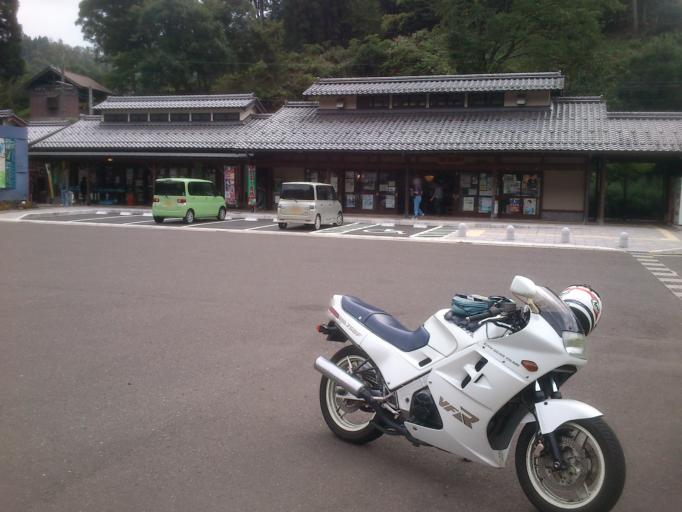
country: JP
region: Fukui
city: Obama
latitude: 35.3950
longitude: 135.5841
